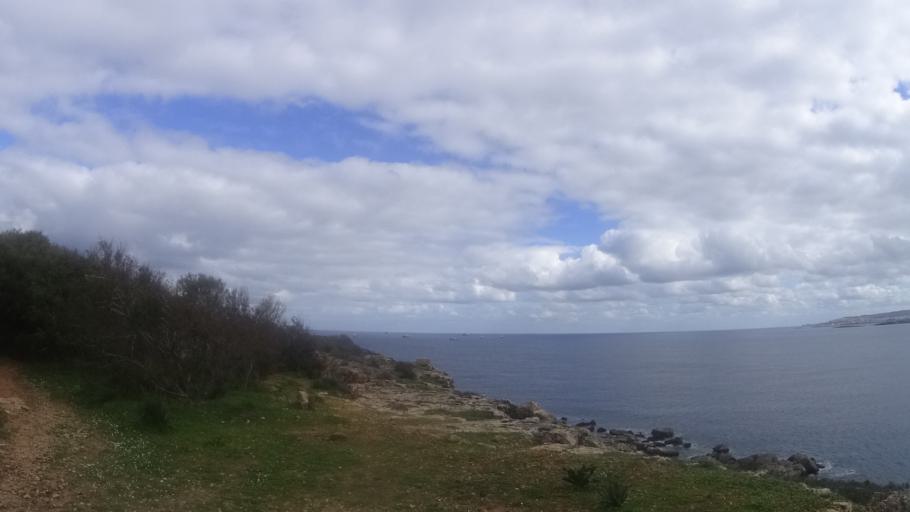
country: MT
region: Il-Mellieha
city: Mellieha
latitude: 35.9865
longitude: 14.3716
